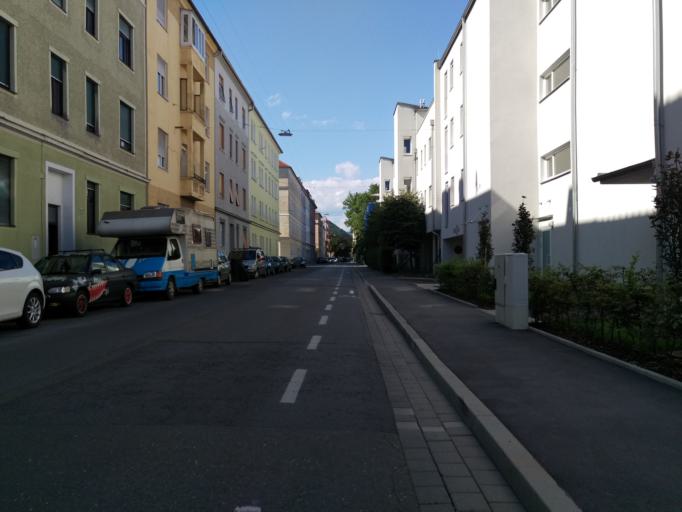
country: AT
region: Styria
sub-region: Graz Stadt
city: Wetzelsdorf
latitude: 47.0648
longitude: 15.4031
